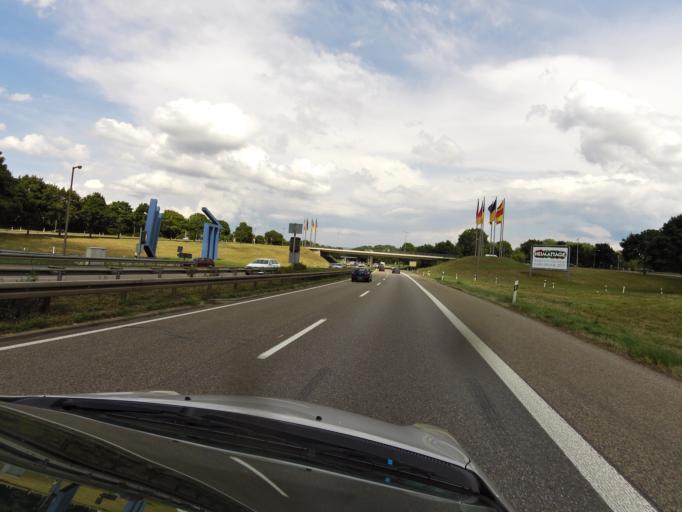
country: DE
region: Baden-Wuerttemberg
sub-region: Karlsruhe Region
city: Karlsruhe
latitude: 48.9894
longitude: 8.4016
